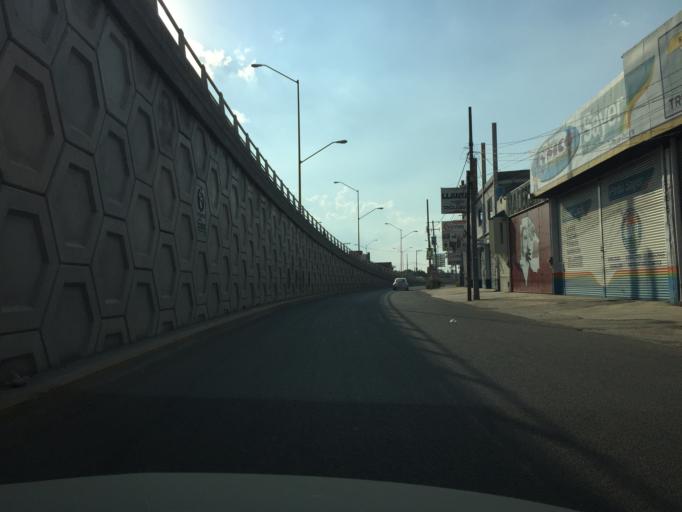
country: MX
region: Aguascalientes
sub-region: Aguascalientes
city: La Loma de los Negritos
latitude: 21.8593
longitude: -102.3145
